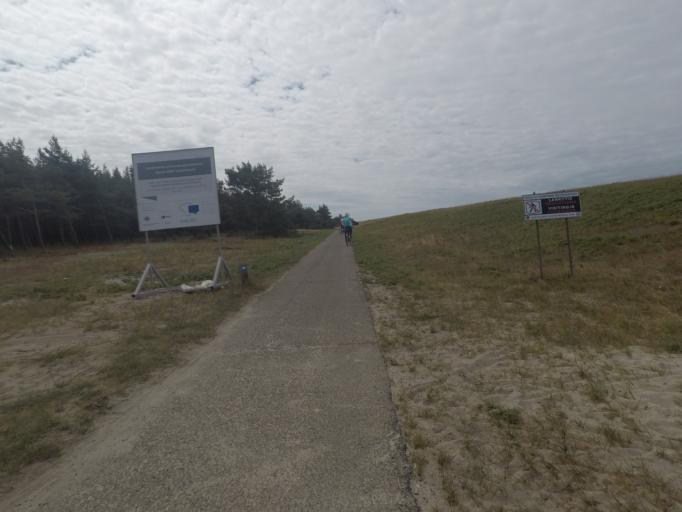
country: LT
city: Neringa
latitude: 55.5167
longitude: 21.0941
